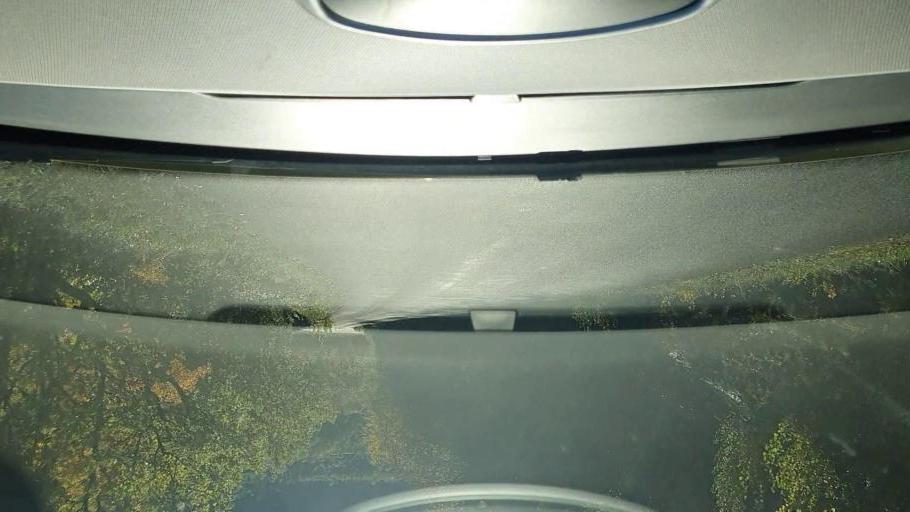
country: FR
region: Languedoc-Roussillon
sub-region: Departement du Gard
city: Le Vigan
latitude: 43.9806
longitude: 3.4963
